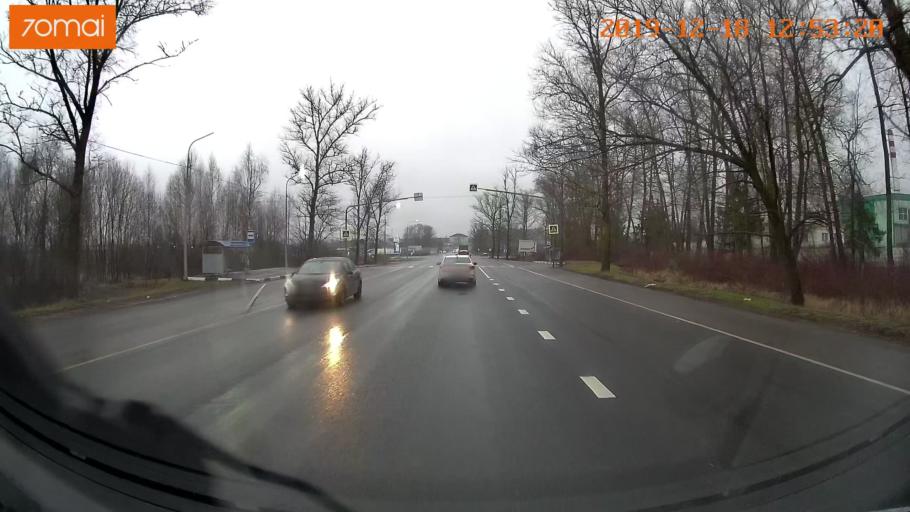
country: RU
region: Moskovskaya
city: Klin
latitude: 56.3182
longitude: 36.6935
